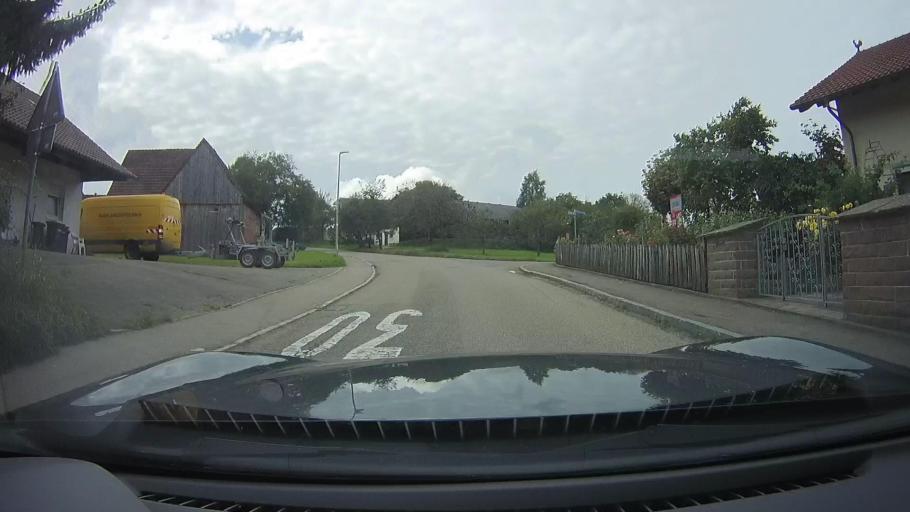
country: DE
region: Baden-Wuerttemberg
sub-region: Regierungsbezirk Stuttgart
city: Althutte
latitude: 48.9442
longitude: 9.5503
